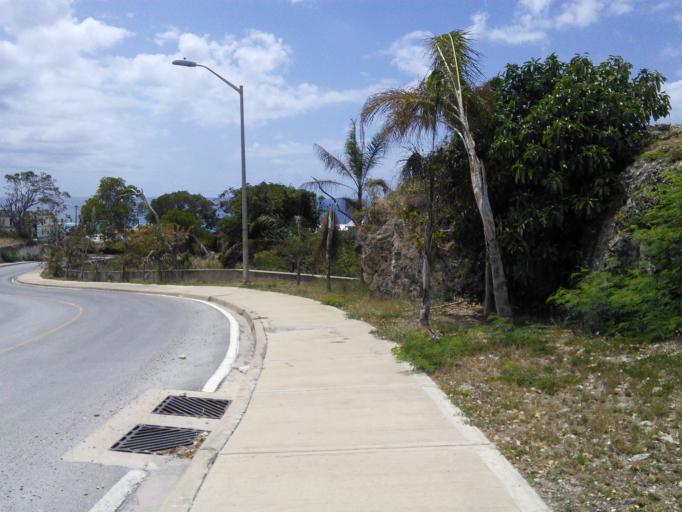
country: BB
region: Saint Michael
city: Bridgetown
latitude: 13.1379
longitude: -59.6345
